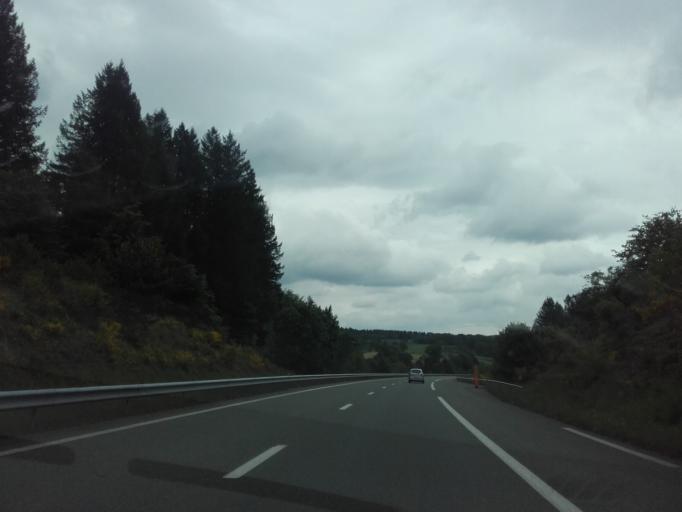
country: FR
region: Limousin
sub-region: Departement de la Correze
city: Correze
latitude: 45.3603
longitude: 1.9340
